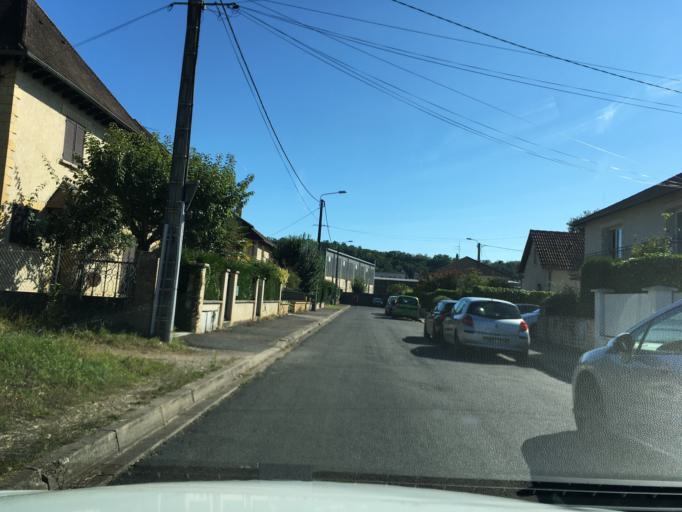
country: FR
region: Limousin
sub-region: Departement de la Correze
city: Brive-la-Gaillarde
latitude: 45.1607
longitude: 1.5203
